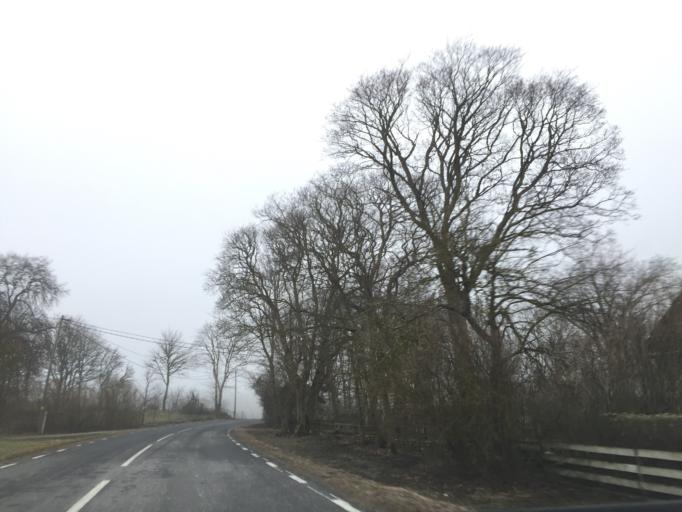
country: EE
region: Saare
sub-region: Kuressaare linn
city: Kuressaare
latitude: 58.4656
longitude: 22.0083
